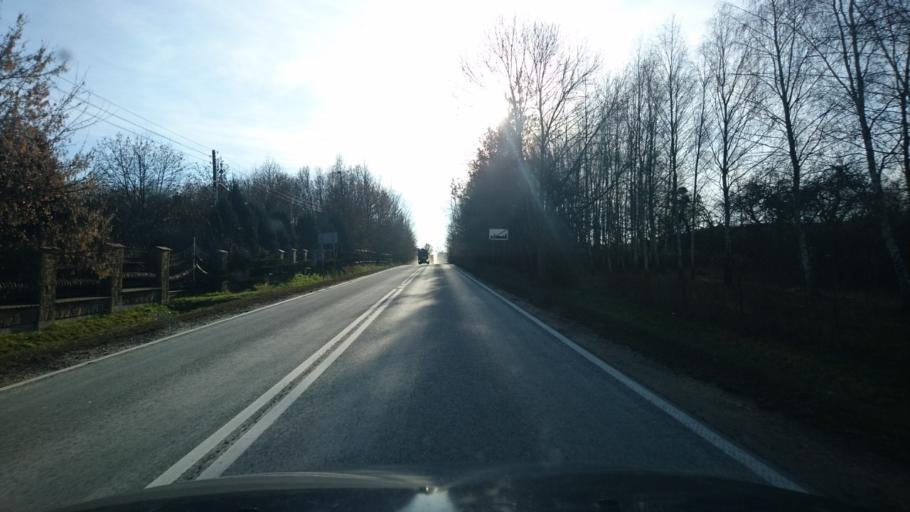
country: PL
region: Opole Voivodeship
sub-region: Powiat oleski
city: Dalachow
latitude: 51.0738
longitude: 18.6022
